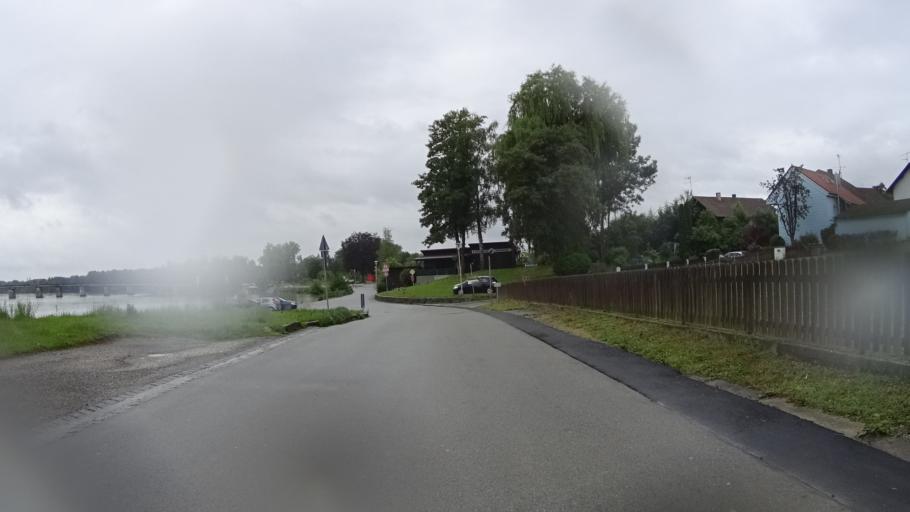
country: AT
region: Upper Austria
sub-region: Politischer Bezirk Scharding
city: Scharding
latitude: 48.4598
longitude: 13.4253
